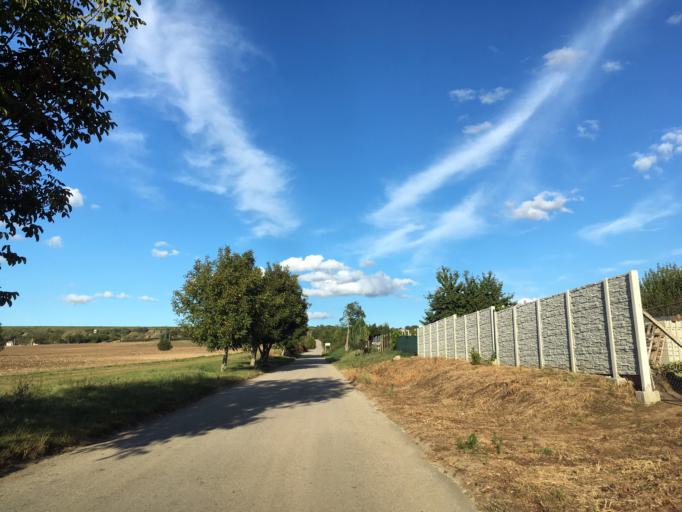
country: SK
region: Nitriansky
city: Svodin
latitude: 47.9088
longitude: 18.4196
